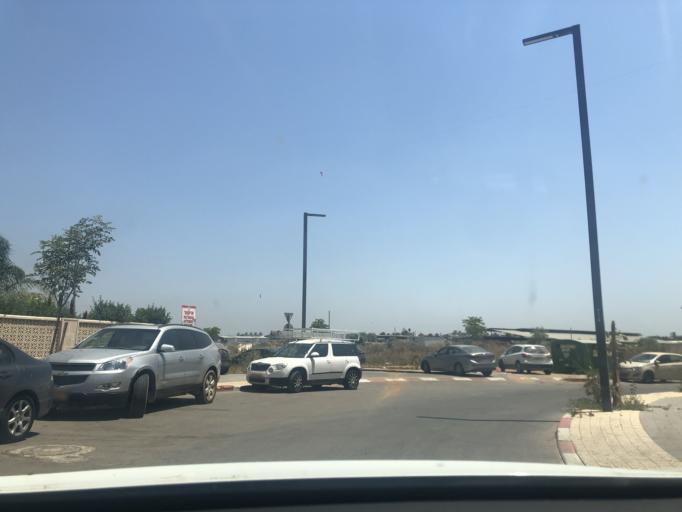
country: IL
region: Central District
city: Lod
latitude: 31.9362
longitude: 34.8993
